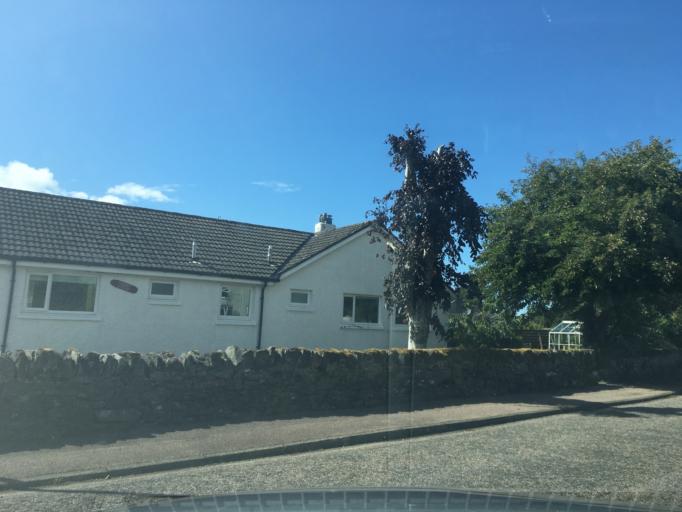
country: GB
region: Scotland
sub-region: Argyll and Bute
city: Lochgilphead
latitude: 56.0807
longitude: -5.4512
